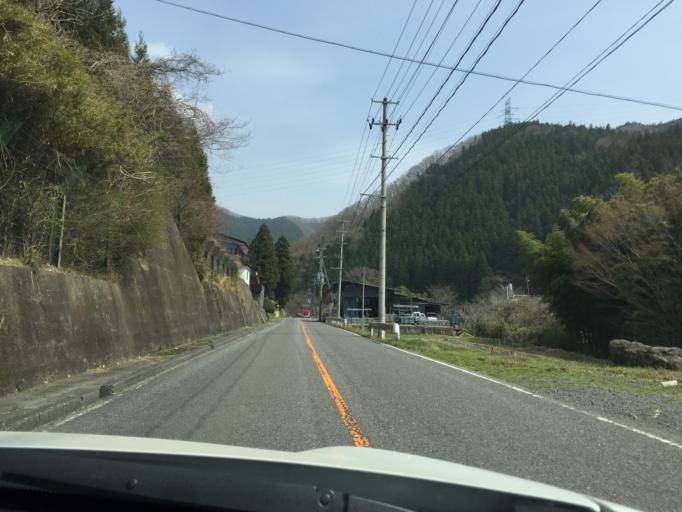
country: JP
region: Fukushima
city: Ishikawa
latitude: 37.0537
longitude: 140.6051
